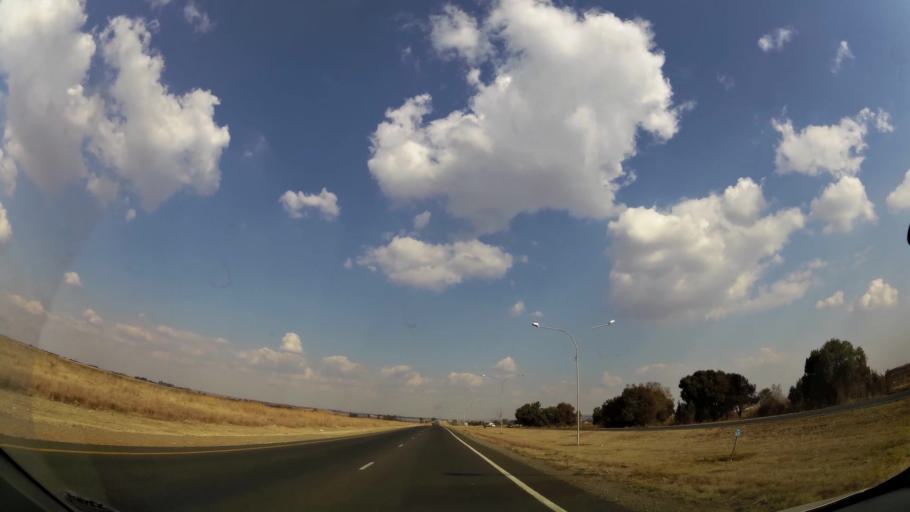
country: ZA
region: Gauteng
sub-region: Ekurhuleni Metropolitan Municipality
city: Brakpan
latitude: -26.2838
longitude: 28.3310
